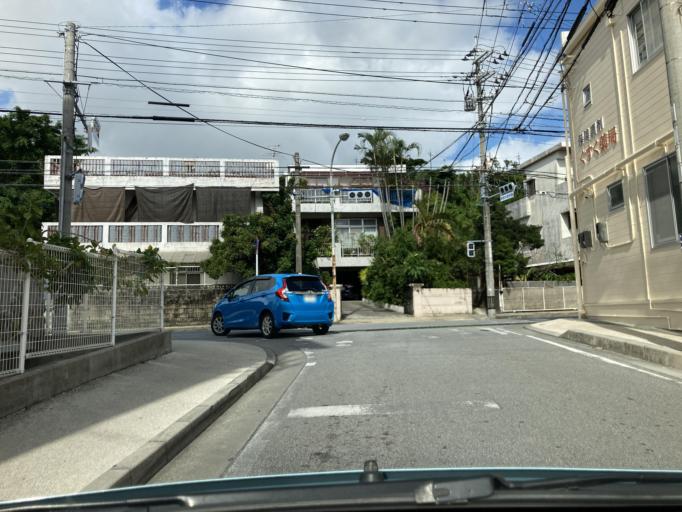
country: JP
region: Okinawa
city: Naha-shi
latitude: 26.2159
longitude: 127.7104
